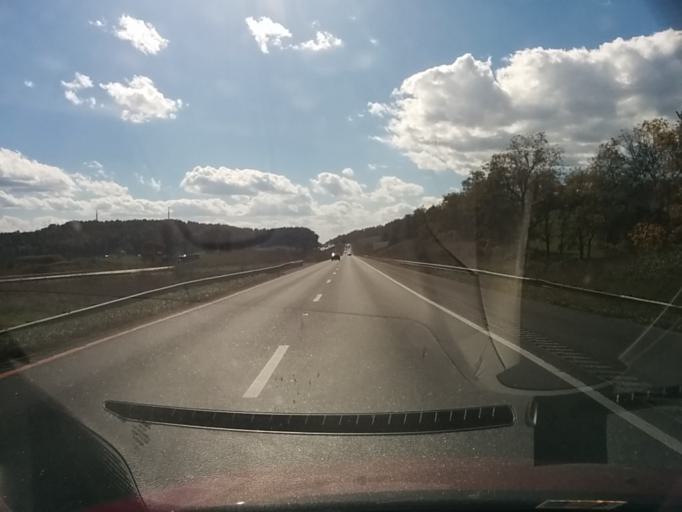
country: US
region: Virginia
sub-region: City of Buena Vista
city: Buena Vista
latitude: 37.9103
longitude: -79.2589
